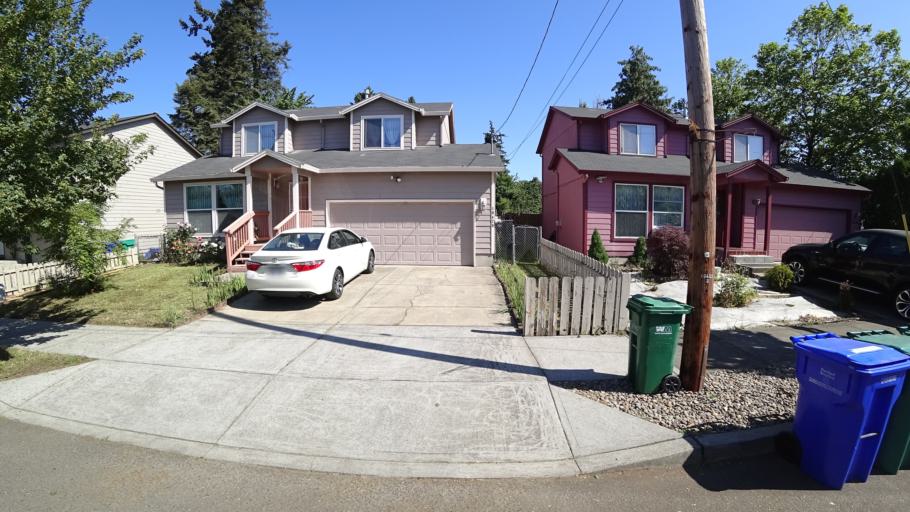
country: US
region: Oregon
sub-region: Multnomah County
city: Lents
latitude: 45.4790
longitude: -122.5550
